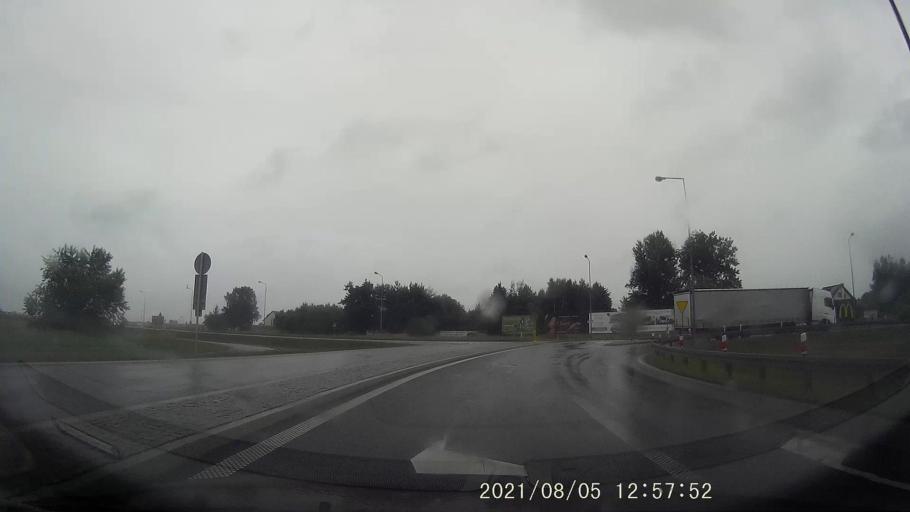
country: PL
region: Opole Voivodeship
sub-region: Powiat krapkowicki
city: Krapkowice
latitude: 50.4819
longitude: 17.9923
